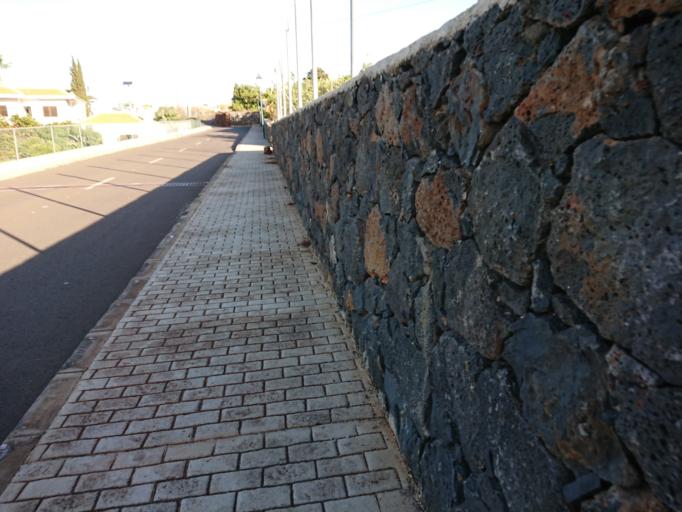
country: ES
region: Canary Islands
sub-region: Provincia de Santa Cruz de Tenerife
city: Tijarafe
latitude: 28.6776
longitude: -17.9449
